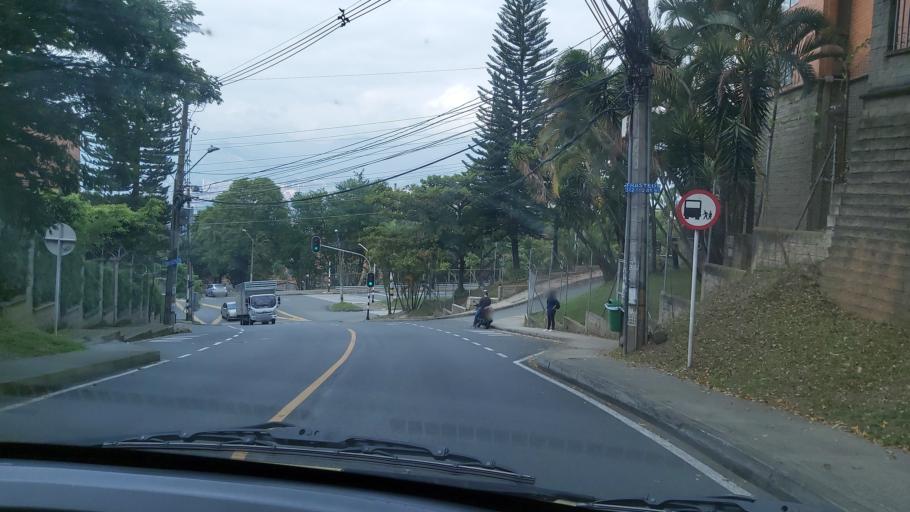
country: CO
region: Antioquia
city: Medellin
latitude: 6.2295
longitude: -75.5634
